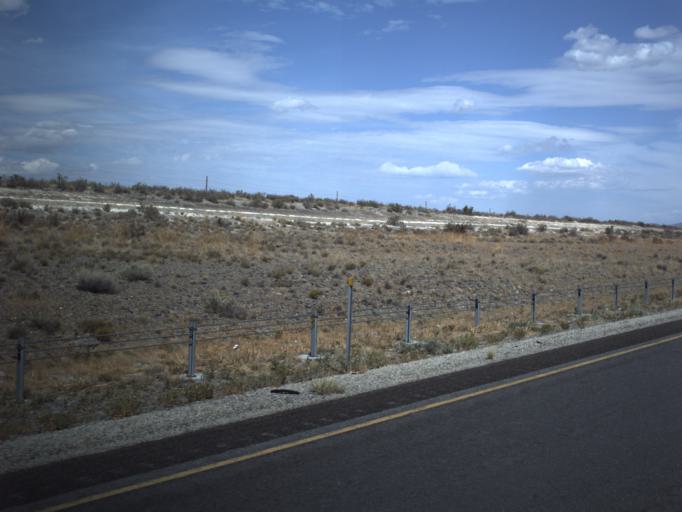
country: US
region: Utah
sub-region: Tooele County
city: Grantsville
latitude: 40.7259
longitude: -113.1349
